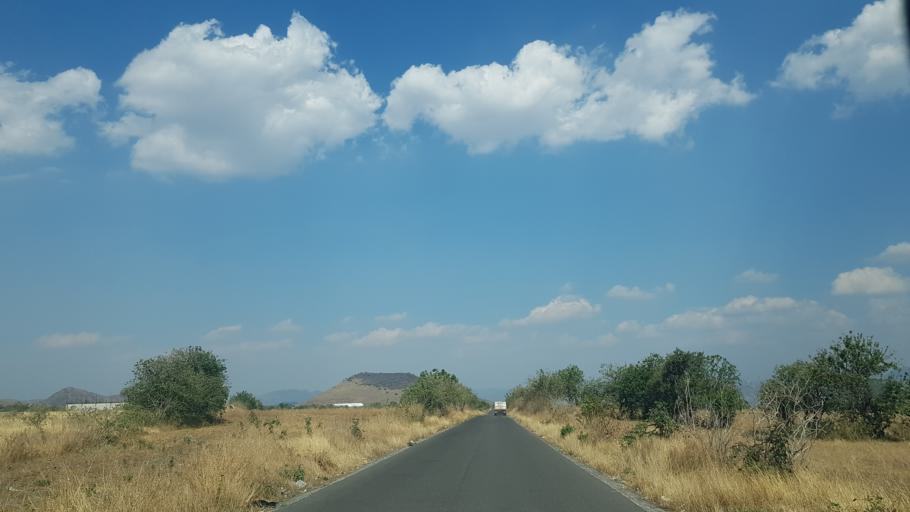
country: MX
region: Puebla
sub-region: Atlixco
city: Colonia Agricola de Ocotepec (Colonia San Jose)
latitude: 18.9236
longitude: -98.5005
